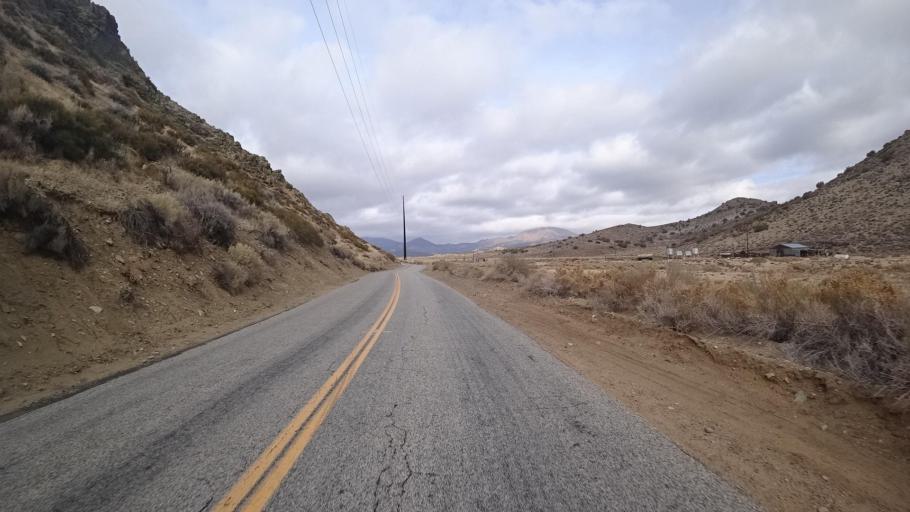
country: US
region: California
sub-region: Kern County
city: Tehachapi
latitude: 35.1496
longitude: -118.3125
